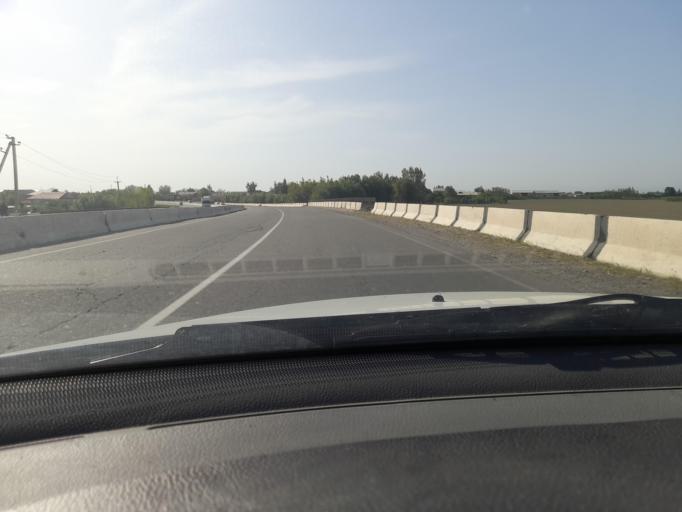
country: UZ
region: Samarqand
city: Kattaqo'rg'on
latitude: 39.9277
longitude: 66.2714
